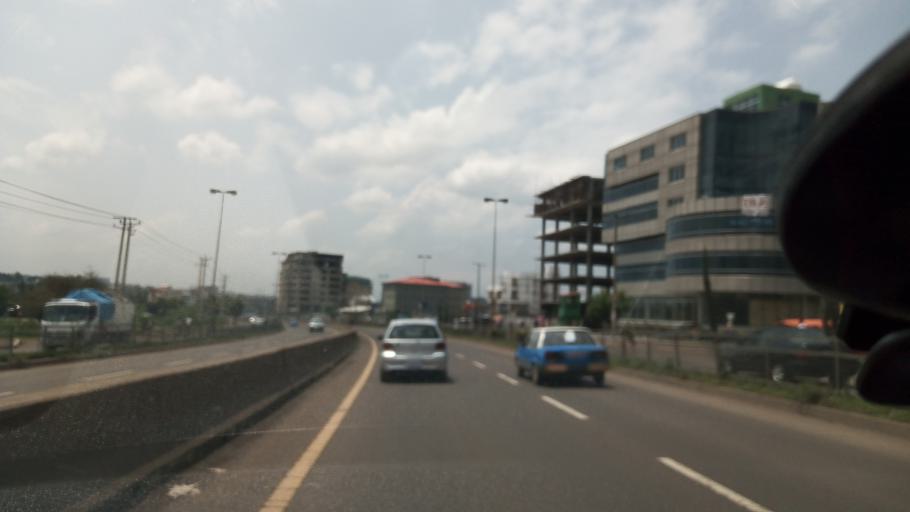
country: ET
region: Adis Abeba
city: Addis Ababa
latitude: 8.9649
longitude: 38.7286
